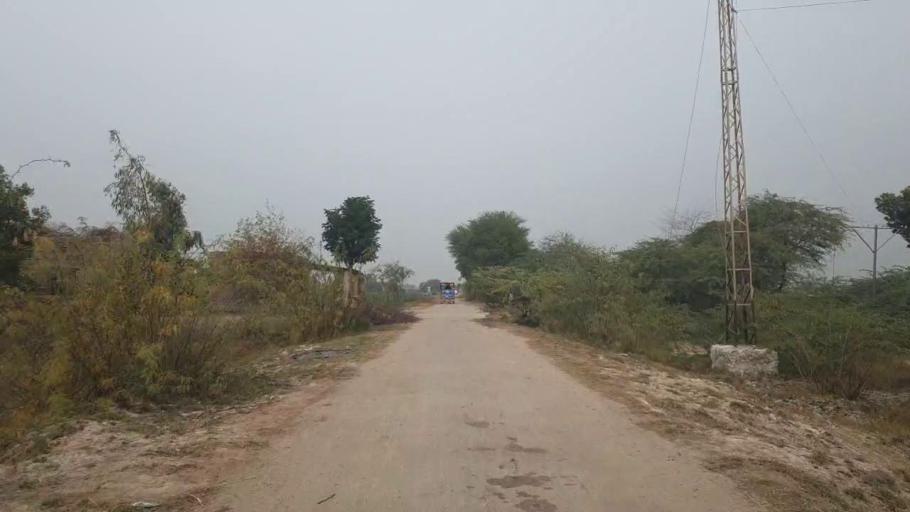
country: PK
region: Sindh
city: Tando Adam
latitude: 25.8470
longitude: 68.6640
